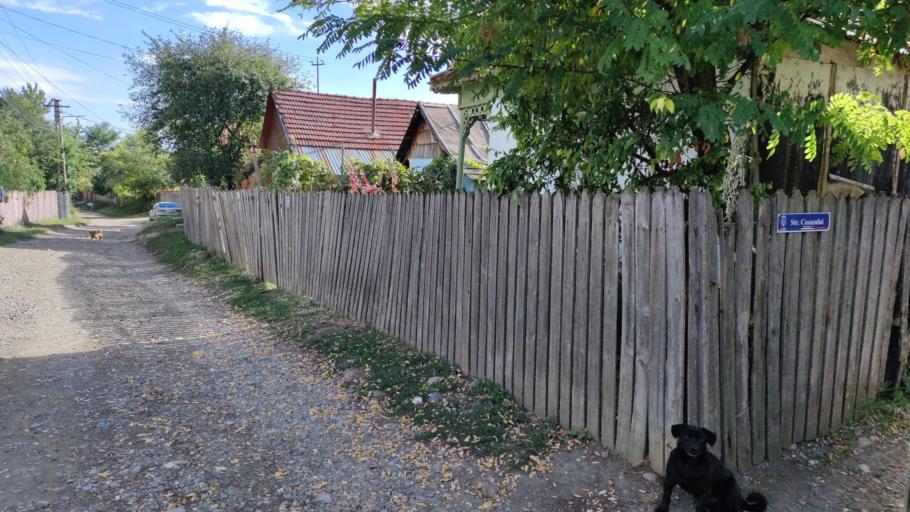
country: RO
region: Buzau
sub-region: Comuna Beceni
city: Valea Parului
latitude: 45.3585
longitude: 26.7651
